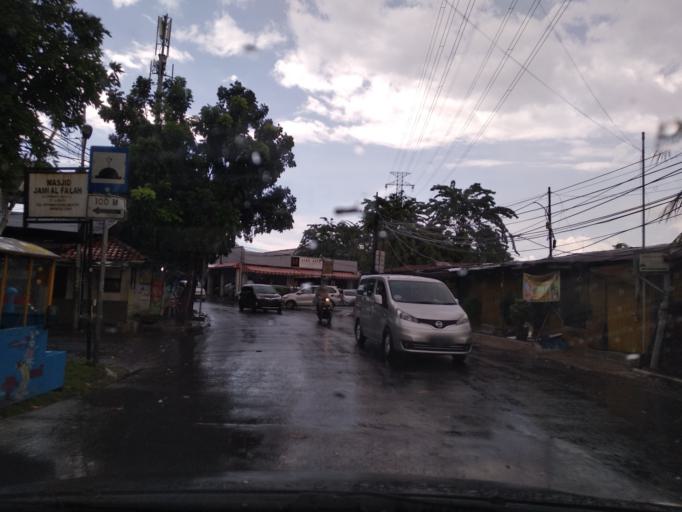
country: ID
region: Jakarta Raya
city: Jakarta
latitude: -6.2186
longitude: 106.8872
